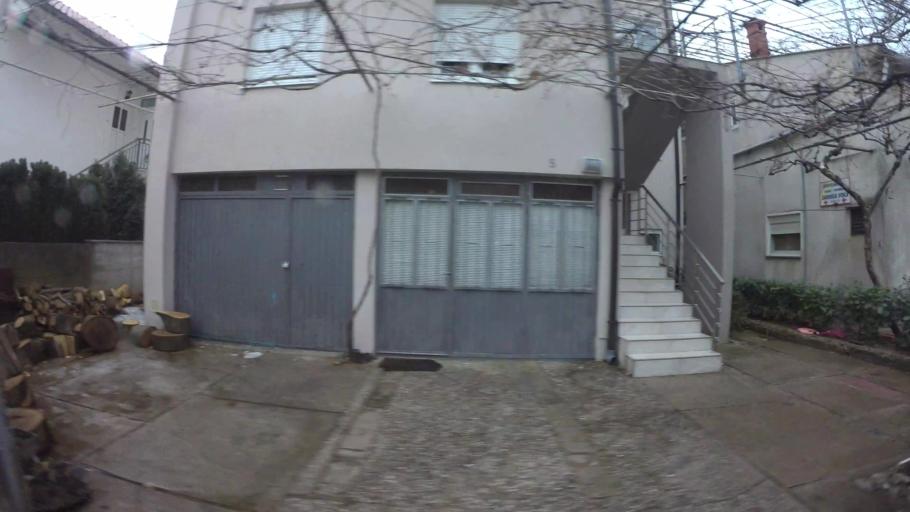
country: BA
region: Federation of Bosnia and Herzegovina
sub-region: Hercegovacko-Bosanski Kanton
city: Mostar
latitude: 43.3574
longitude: 17.8002
